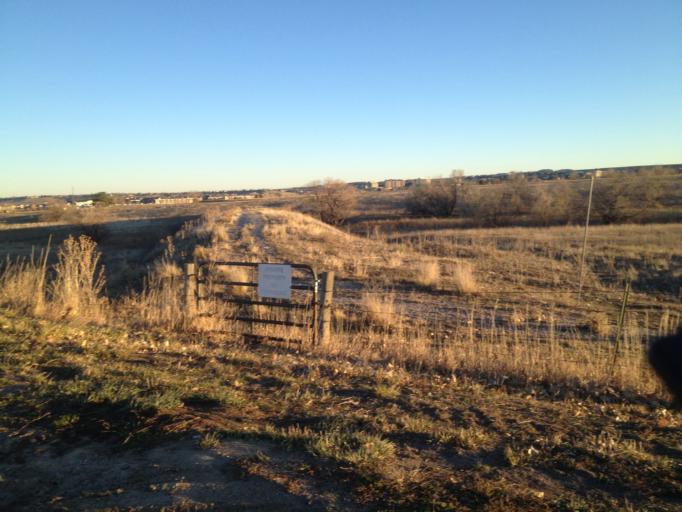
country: US
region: Colorado
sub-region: Boulder County
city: Louisville
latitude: 39.9507
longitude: -105.1391
